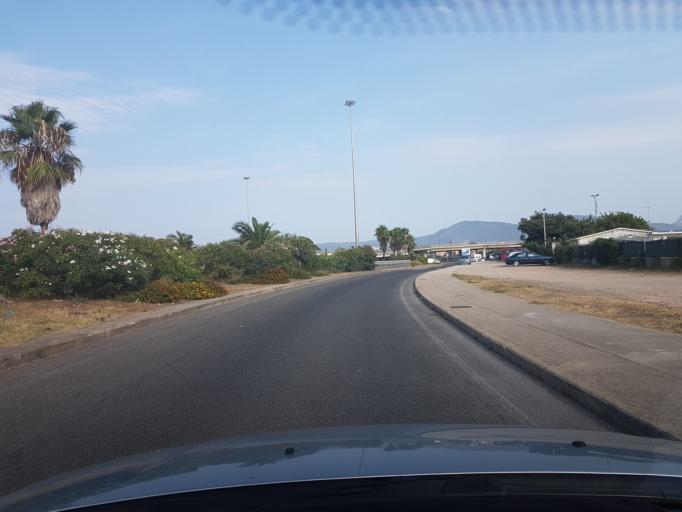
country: IT
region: Sardinia
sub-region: Provincia di Olbia-Tempio
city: Olbia
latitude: 40.9251
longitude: 9.5094
